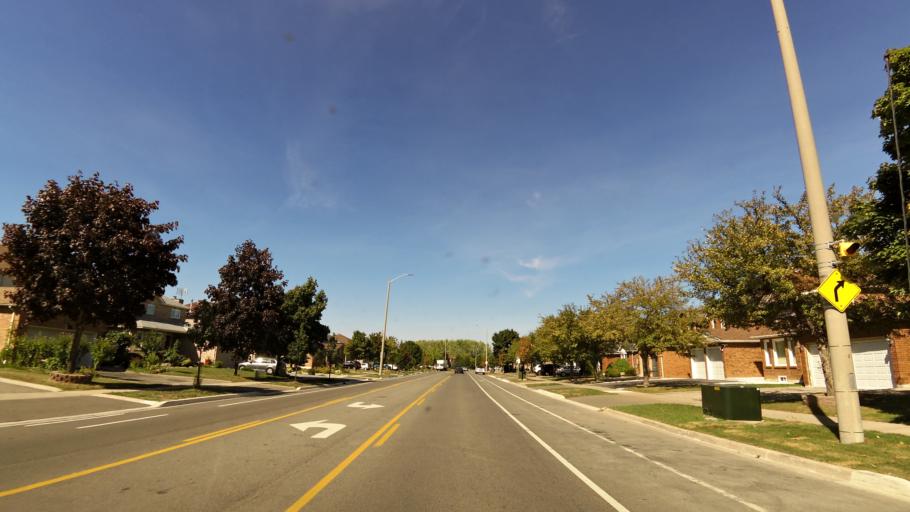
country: CA
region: Ontario
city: Mississauga
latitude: 43.6066
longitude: -79.6695
